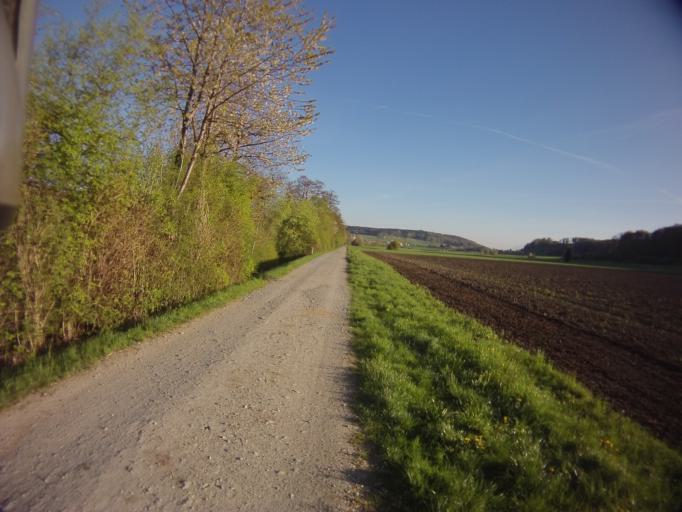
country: CH
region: Zurich
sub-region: Bezirk Affoltern
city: Wettswil / Wettswil (Dorf)
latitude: 47.3348
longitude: 8.4654
